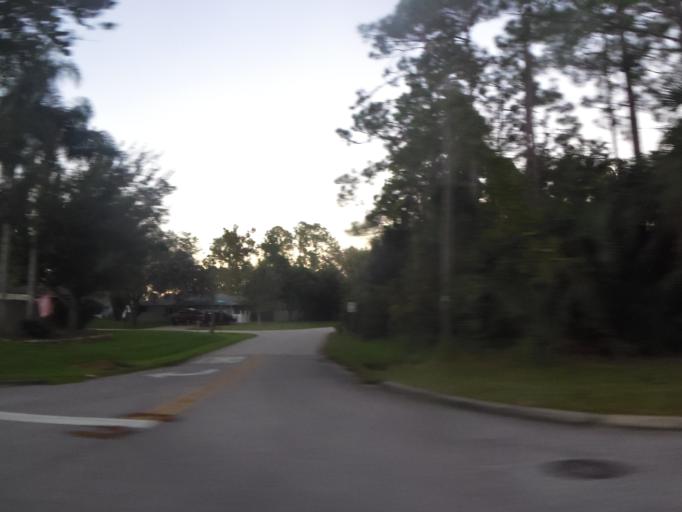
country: US
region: Florida
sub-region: Flagler County
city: Palm Coast
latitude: 29.5648
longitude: -81.2435
